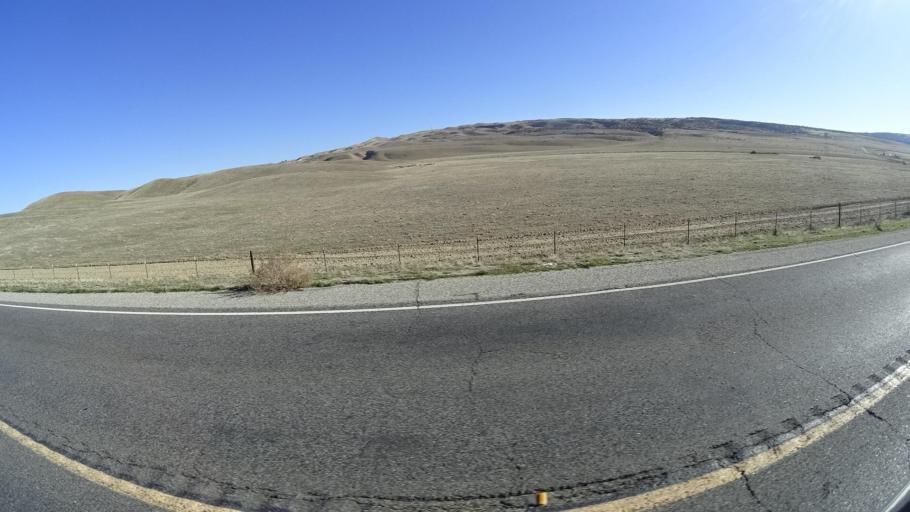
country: US
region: California
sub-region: Kern County
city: Maricopa
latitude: 34.9484
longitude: -119.4550
